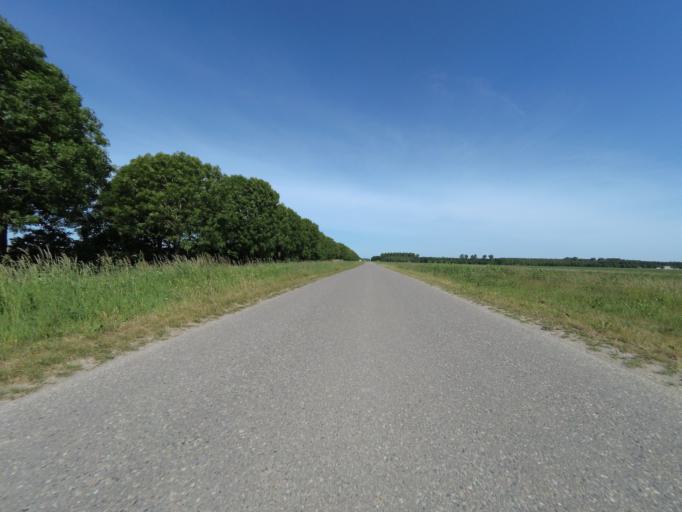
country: NL
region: Utrecht
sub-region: Gemeente Bunschoten
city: Spakenburg
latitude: 52.3244
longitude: 5.3374
